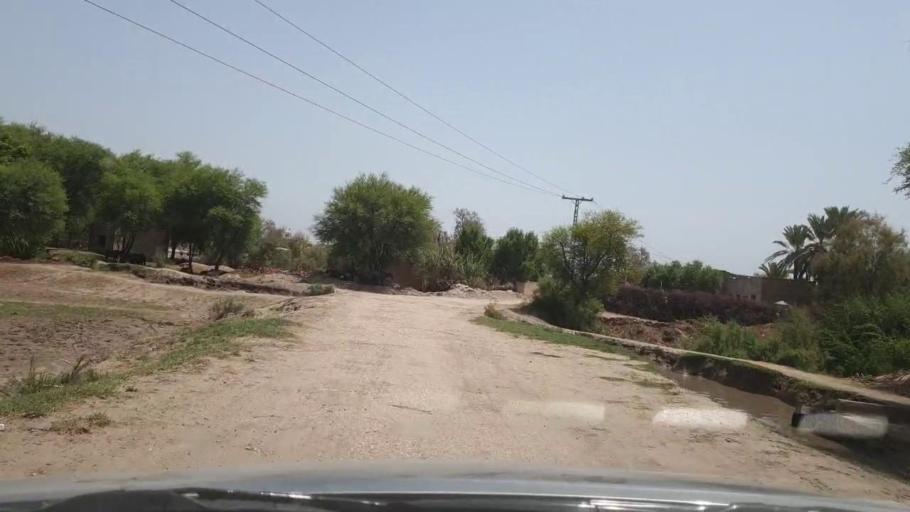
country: PK
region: Sindh
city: Pano Aqil
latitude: 27.8158
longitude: 69.2307
